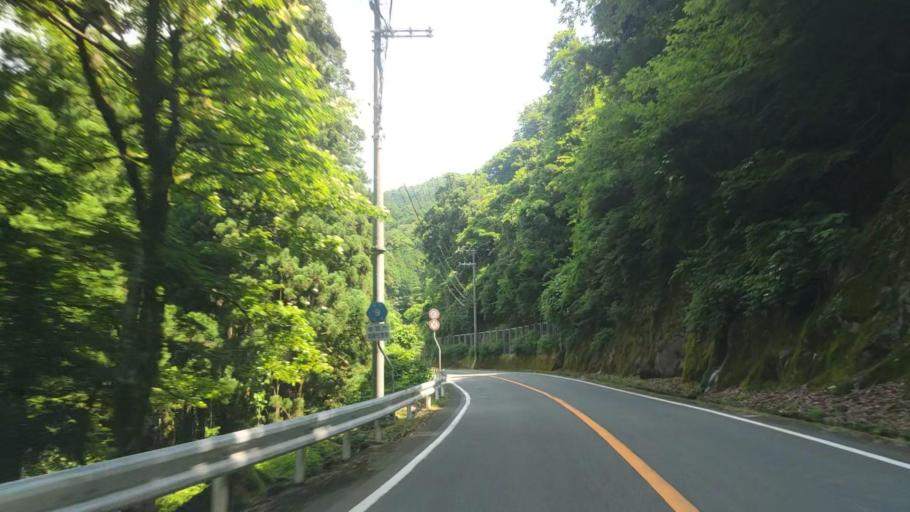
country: JP
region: Hyogo
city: Toyooka
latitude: 35.6340
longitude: 134.7805
